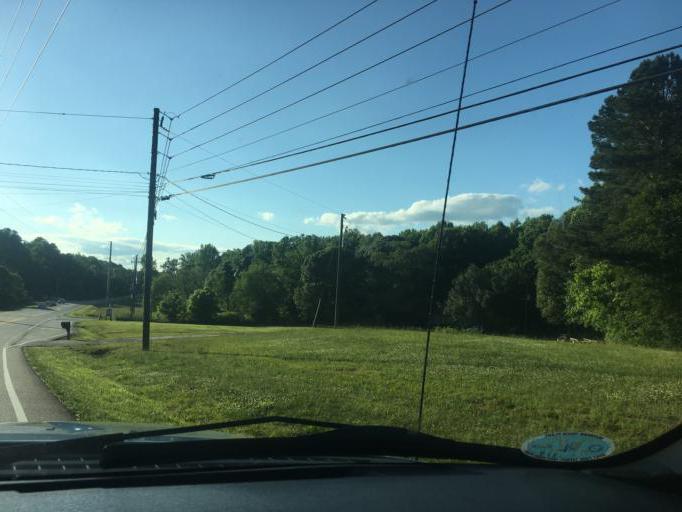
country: US
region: Georgia
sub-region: Forsyth County
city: Cumming
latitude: 34.2746
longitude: -84.1119
